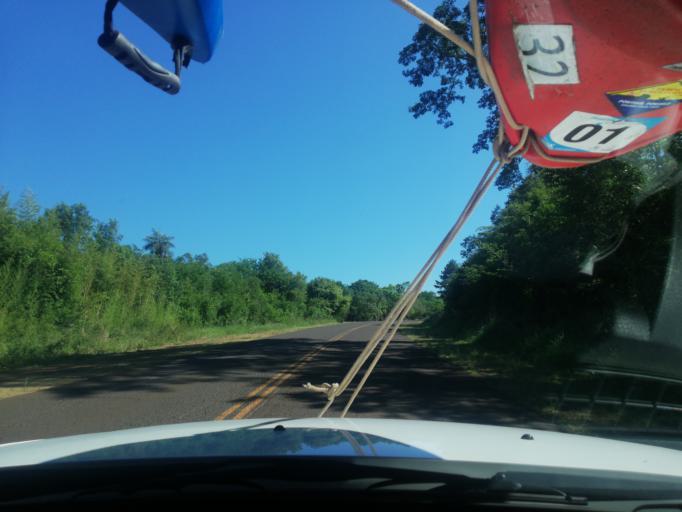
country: AR
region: Misiones
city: Santa Ana
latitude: -27.3577
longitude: -55.5870
